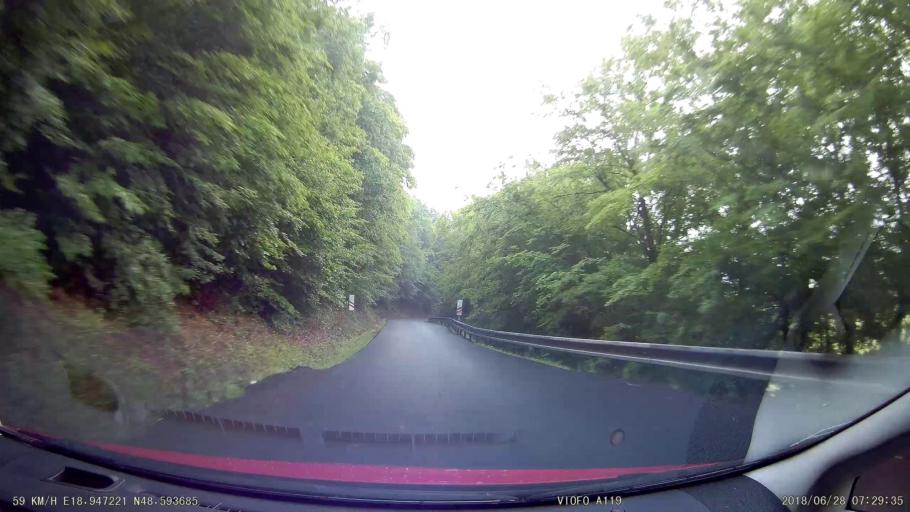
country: SK
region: Banskobystricky
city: Ziar nad Hronom
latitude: 48.5937
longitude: 18.9472
